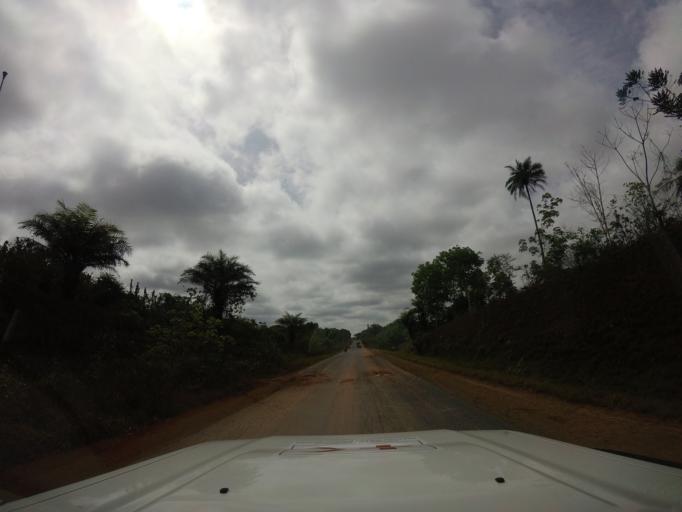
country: LR
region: Montserrado
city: Monrovia
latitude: 6.5298
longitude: -10.8482
